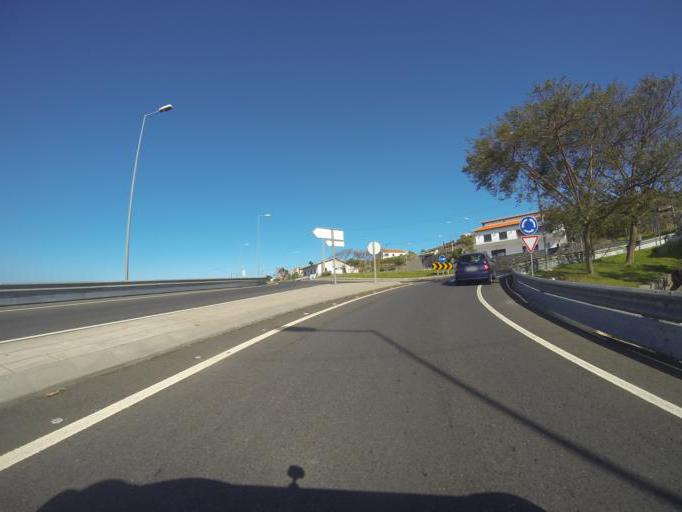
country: PT
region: Madeira
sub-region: Calheta
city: Estreito da Calheta
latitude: 32.7349
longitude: -17.1955
